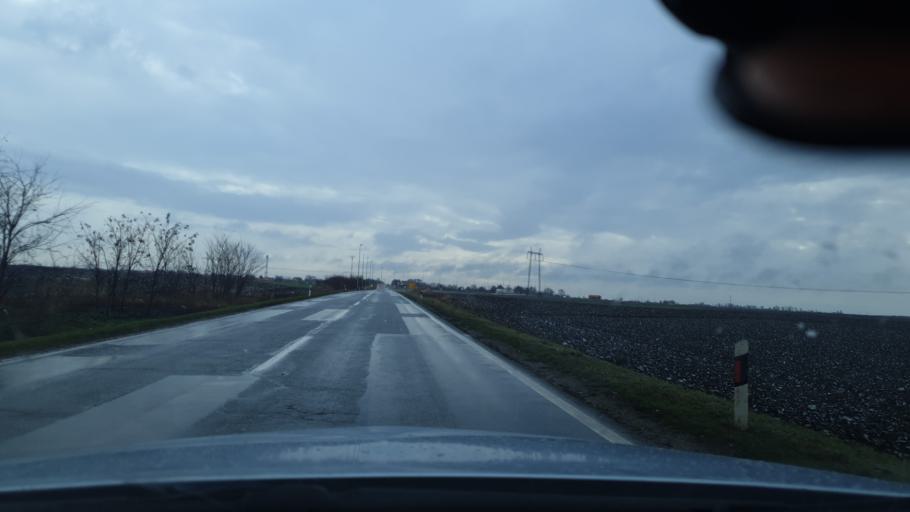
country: RS
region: Autonomna Pokrajina Vojvodina
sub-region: Juznobanatski Okrug
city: Kovin
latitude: 44.8268
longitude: 20.8453
